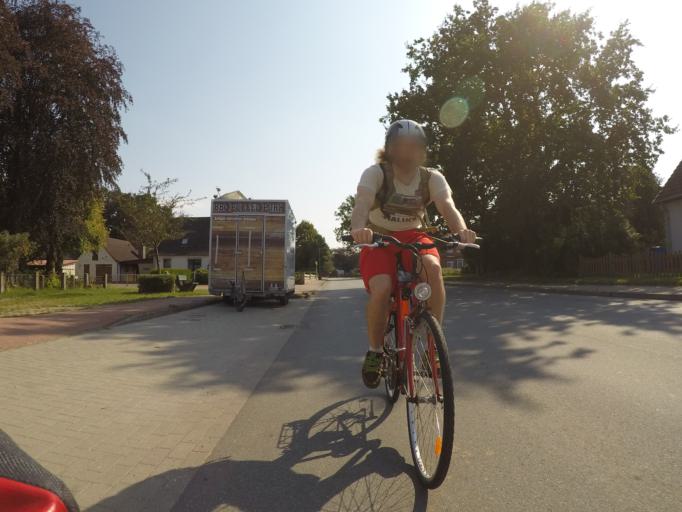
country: DE
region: Schleswig-Holstein
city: Todesfelde
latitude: 53.8924
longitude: 10.1764
